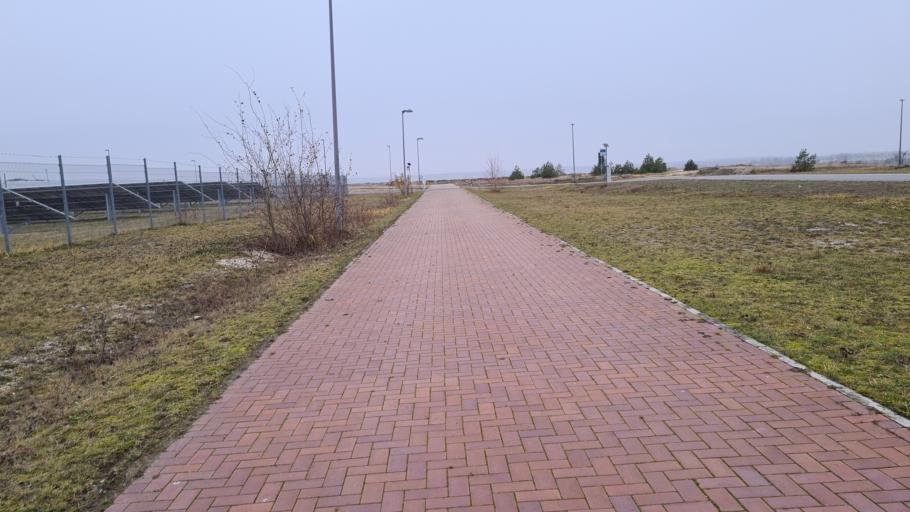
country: DE
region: Brandenburg
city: Sallgast
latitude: 51.5847
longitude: 13.7798
